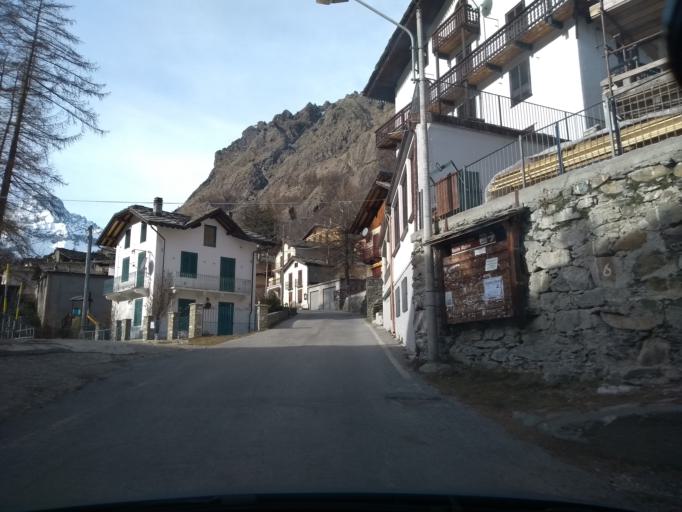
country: IT
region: Piedmont
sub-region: Provincia di Torino
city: Balme
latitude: 45.3023
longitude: 7.2178
